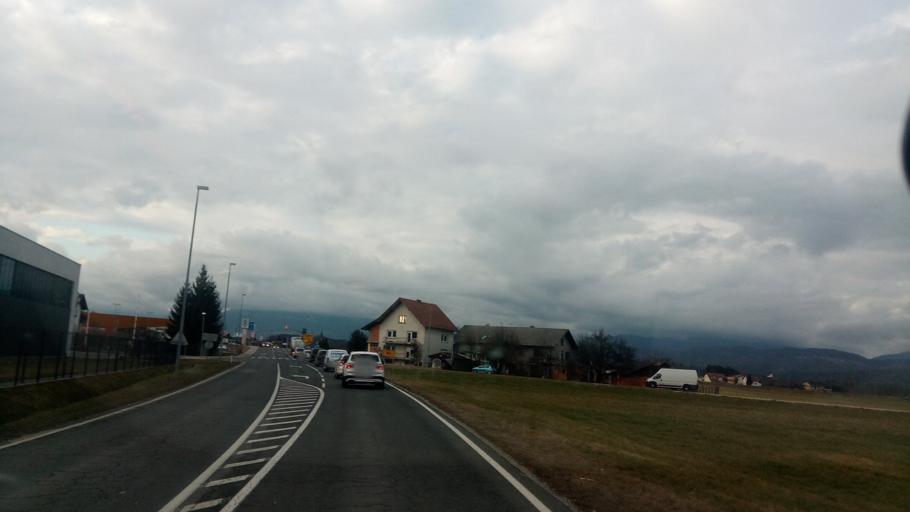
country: SI
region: Domzale
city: Vir
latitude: 46.1482
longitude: 14.6174
